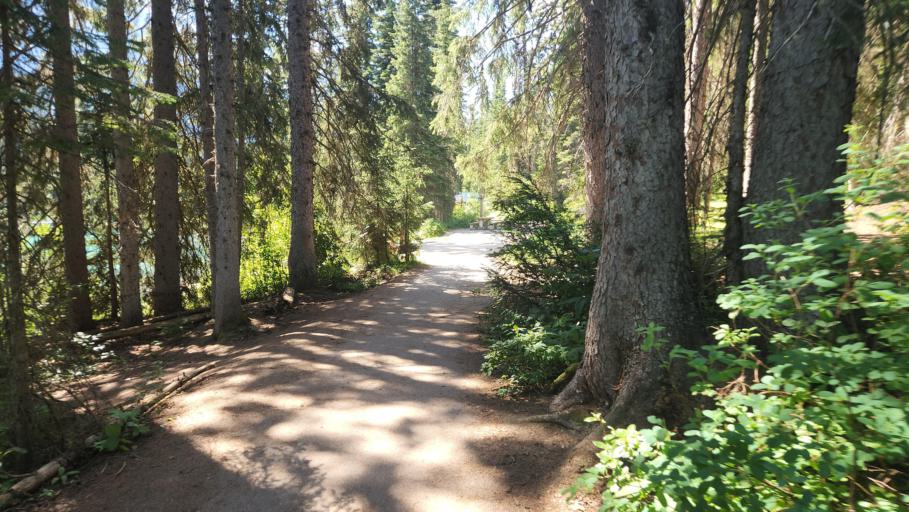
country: CA
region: Alberta
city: Lake Louise
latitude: 51.4407
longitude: -116.5422
